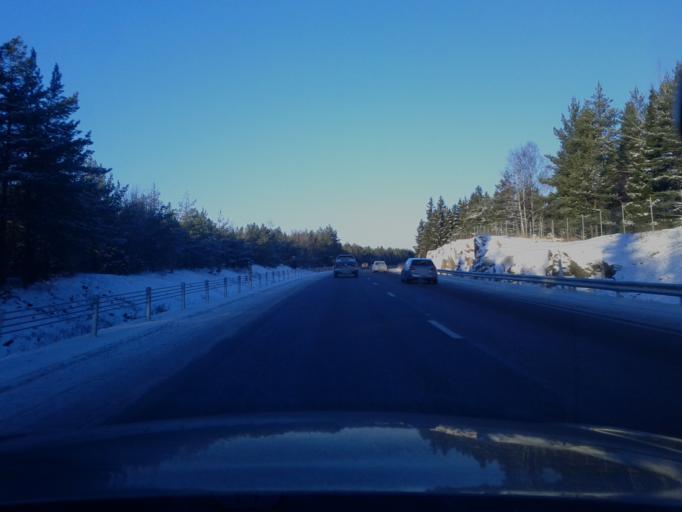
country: SE
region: Uppsala
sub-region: Knivsta Kommun
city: Knivsta
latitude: 59.7637
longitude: 17.7939
